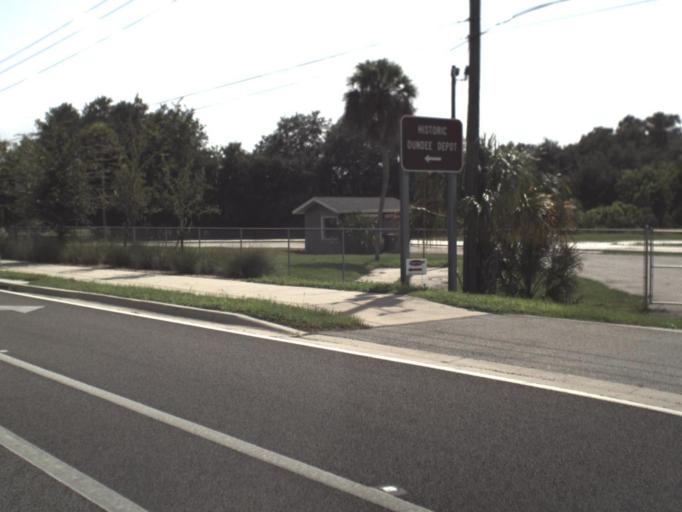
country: US
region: Florida
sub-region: Polk County
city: Dundee
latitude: 28.0204
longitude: -81.6330
